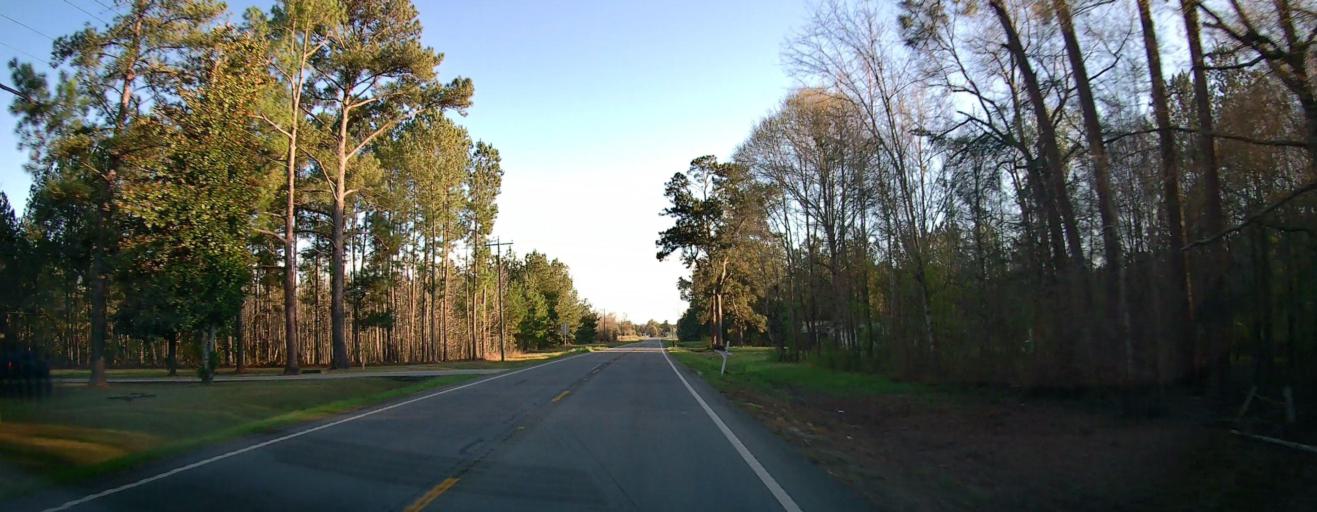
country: US
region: Georgia
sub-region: Wilcox County
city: Abbeville
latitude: 32.0059
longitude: -83.2474
